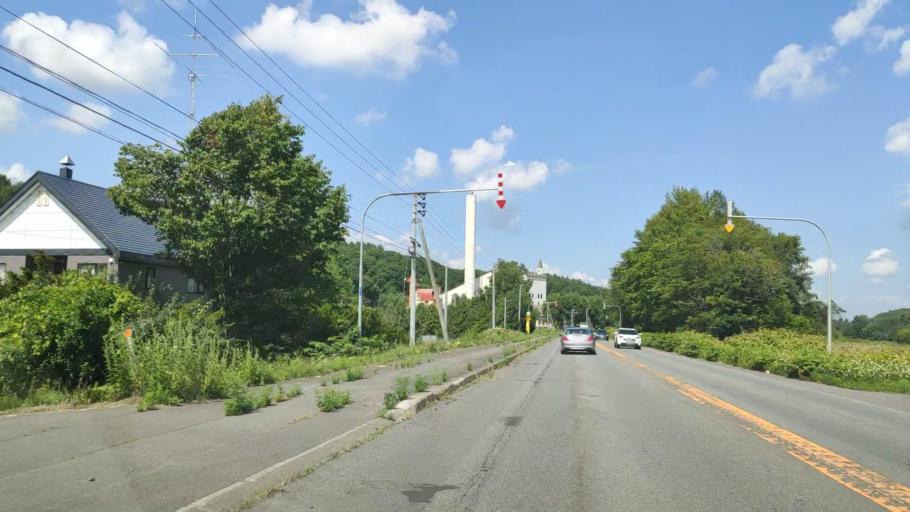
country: JP
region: Hokkaido
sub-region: Asahikawa-shi
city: Asahikawa
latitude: 43.6198
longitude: 142.4717
